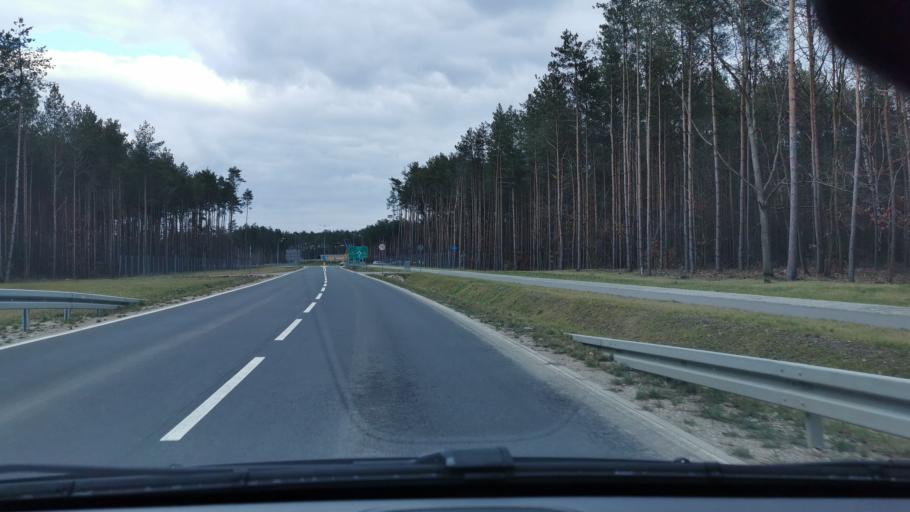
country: PL
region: Masovian Voivodeship
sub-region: Powiat zyrardowski
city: Zyrardow
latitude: 52.0124
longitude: 20.4746
